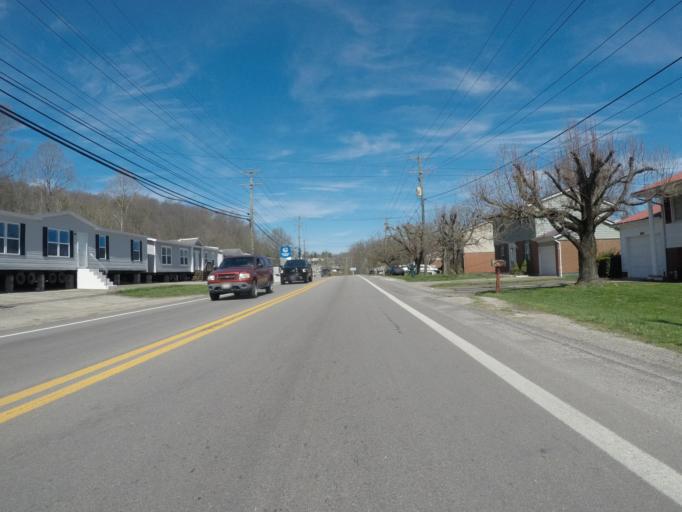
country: US
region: West Virginia
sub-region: Cabell County
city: Pea Ridge
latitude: 38.4036
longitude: -82.3198
